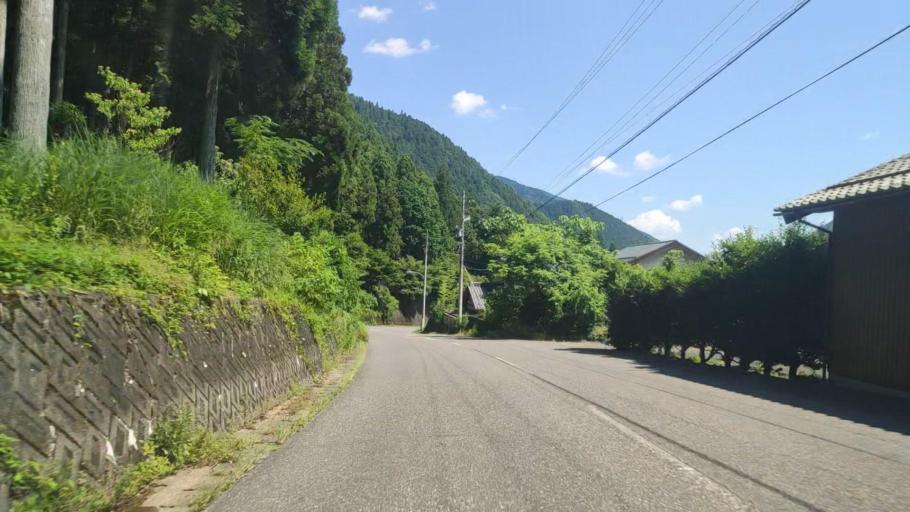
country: JP
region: Gifu
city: Godo
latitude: 35.6281
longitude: 136.6188
